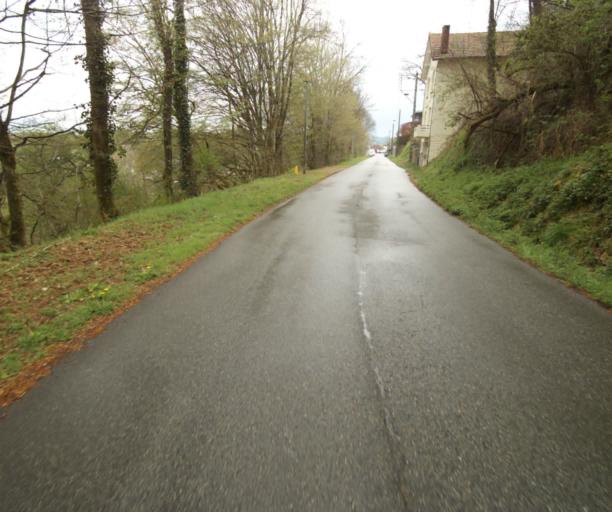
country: FR
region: Limousin
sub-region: Departement de la Correze
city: Tulle
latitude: 45.2683
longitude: 1.7616
